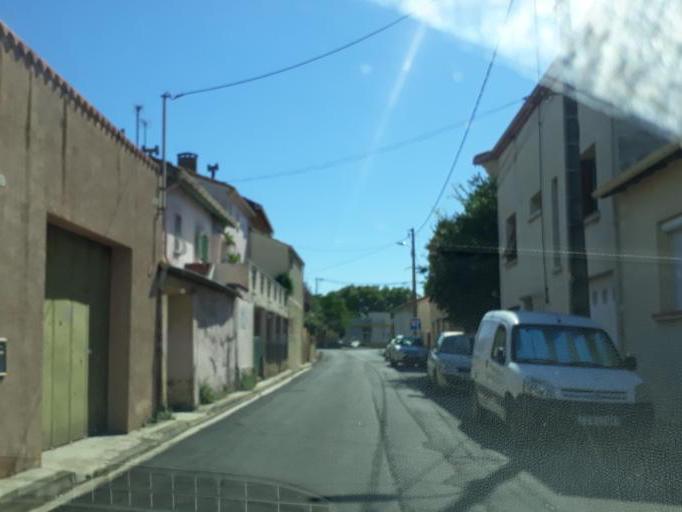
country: FR
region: Languedoc-Roussillon
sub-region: Departement de l'Herault
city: Pezenas
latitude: 43.4565
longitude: 3.4268
